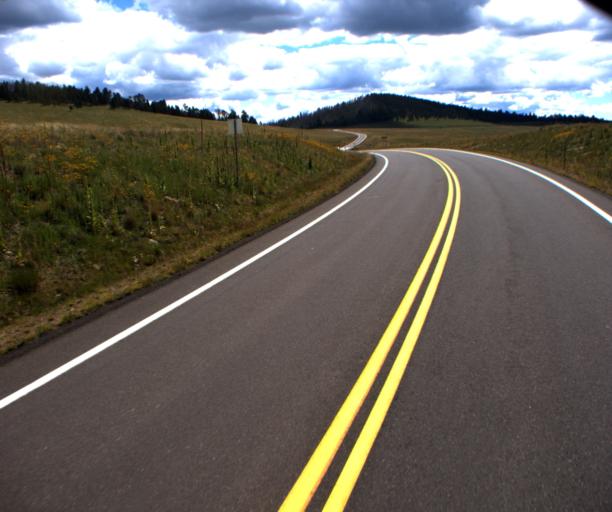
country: US
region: Arizona
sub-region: Apache County
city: Eagar
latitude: 33.9192
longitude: -109.4289
